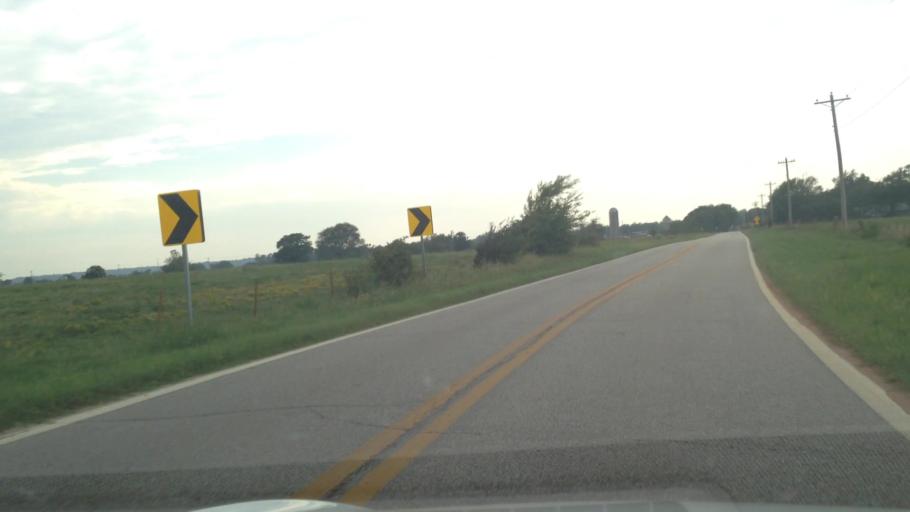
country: US
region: Oklahoma
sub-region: Delaware County
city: Cleora
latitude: 36.5980
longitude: -94.9643
